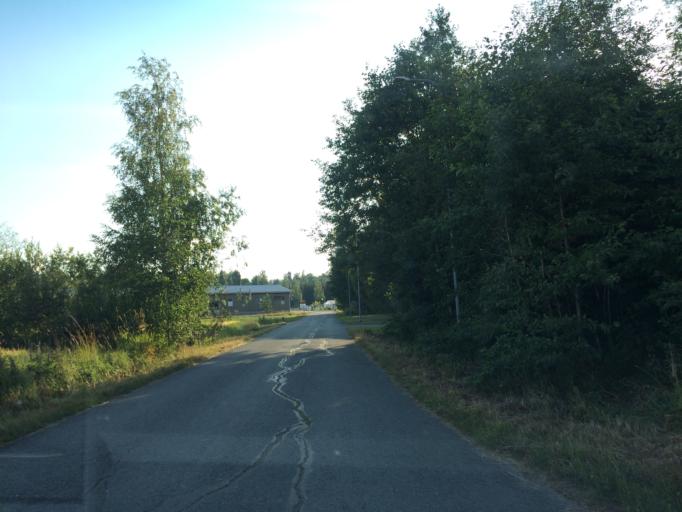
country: FI
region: Haeme
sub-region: Haemeenlinna
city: Parola
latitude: 61.0371
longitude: 24.4124
